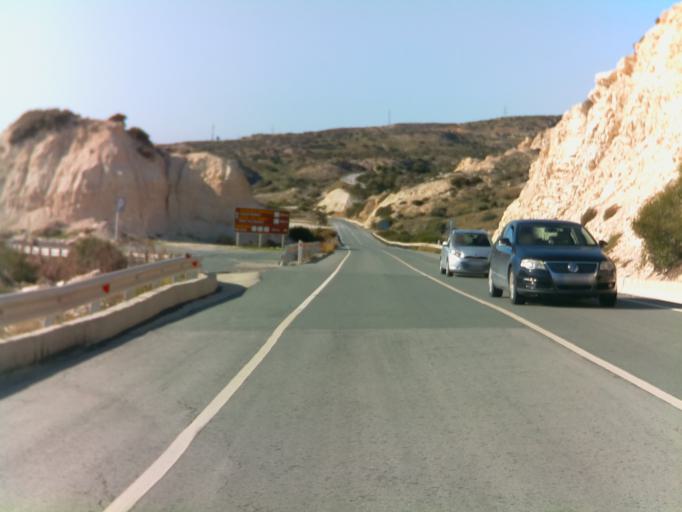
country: CY
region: Limassol
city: Pissouri
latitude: 34.6638
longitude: 32.6378
